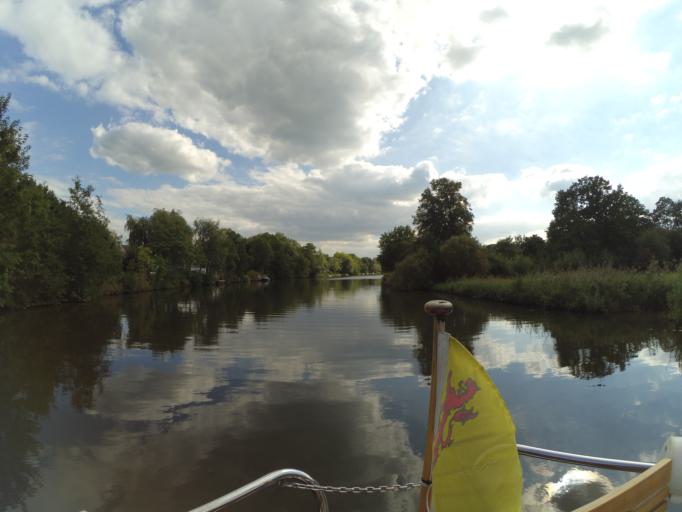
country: NL
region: Utrecht
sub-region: Stichtse Vecht
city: Breukelen
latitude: 52.1693
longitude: 5.0086
